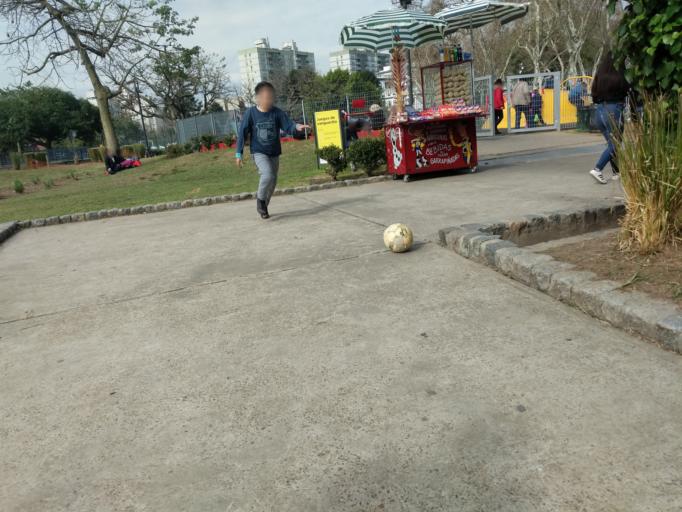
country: AR
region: Buenos Aires F.D.
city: Colegiales
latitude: -34.6052
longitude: -58.4348
